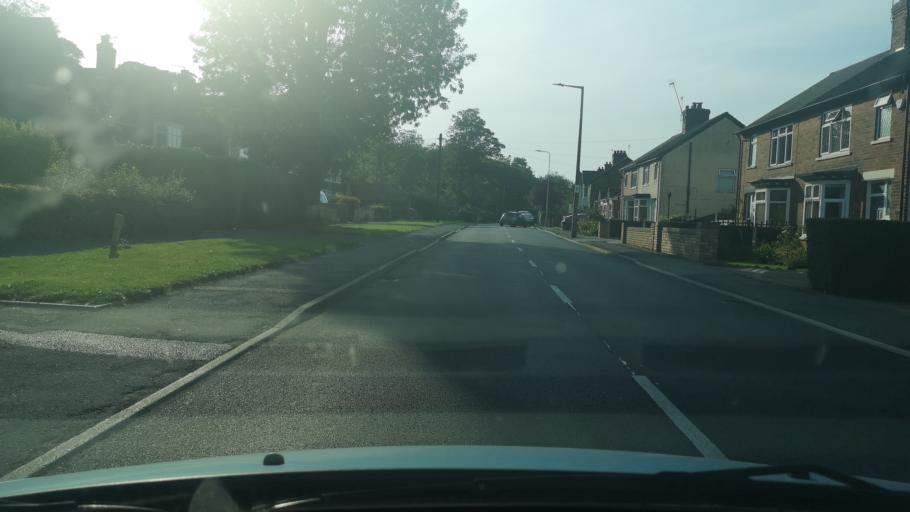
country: GB
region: England
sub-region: North Lincolnshire
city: Scunthorpe
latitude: 53.5844
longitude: -0.6644
